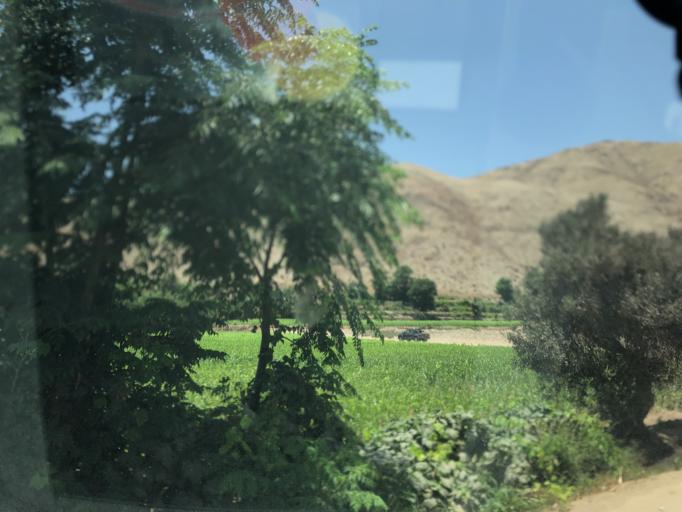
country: PE
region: Lima
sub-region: Provincia de Canete
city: Quilmana
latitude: -12.9816
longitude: -76.4302
